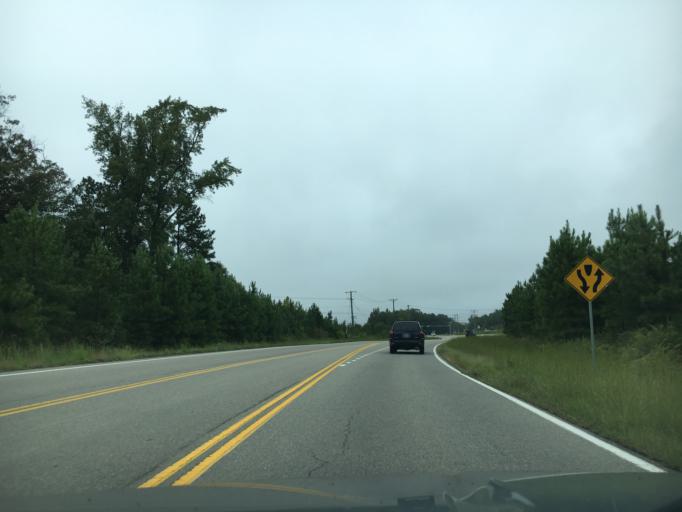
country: US
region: Virginia
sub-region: Chesterfield County
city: Woodlake
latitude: 37.5081
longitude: -77.7759
